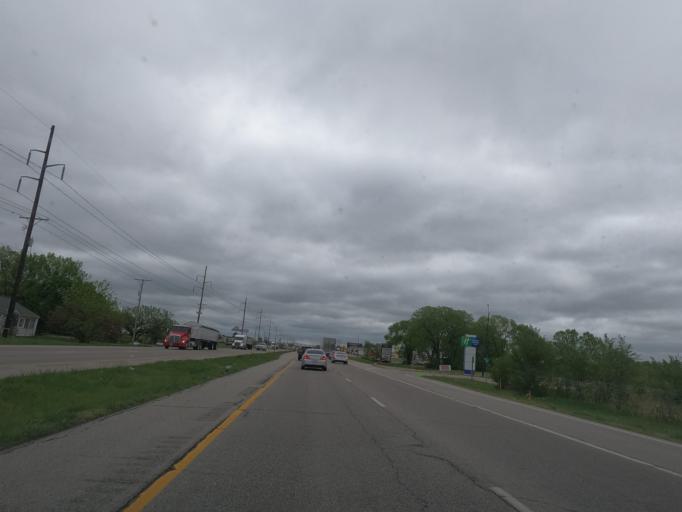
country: US
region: Kansas
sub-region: Butler County
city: Andover
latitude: 37.6795
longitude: -97.1403
